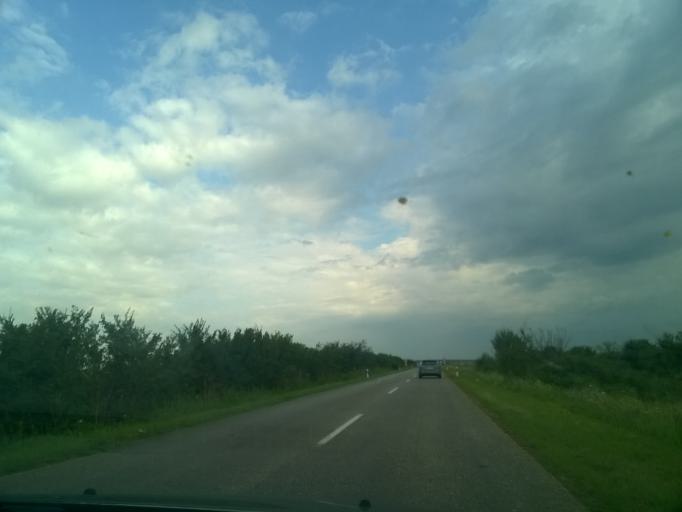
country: RS
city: Uzdin
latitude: 45.2261
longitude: 20.6274
